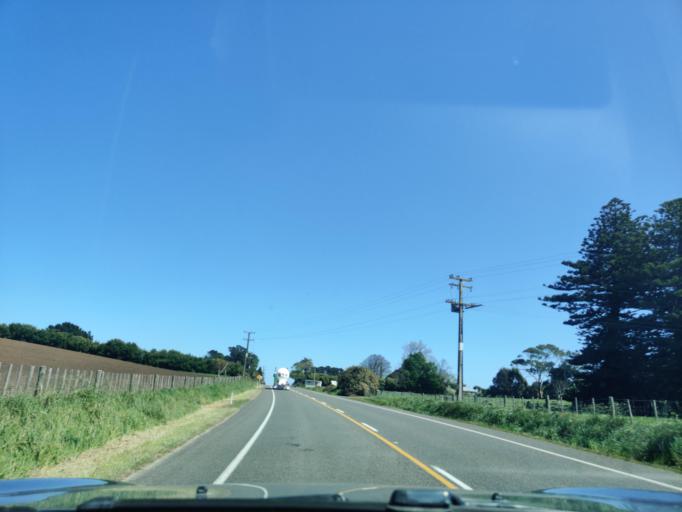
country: NZ
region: Manawatu-Wanganui
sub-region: Wanganui District
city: Wanganui
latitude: -39.8213
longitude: 174.8664
